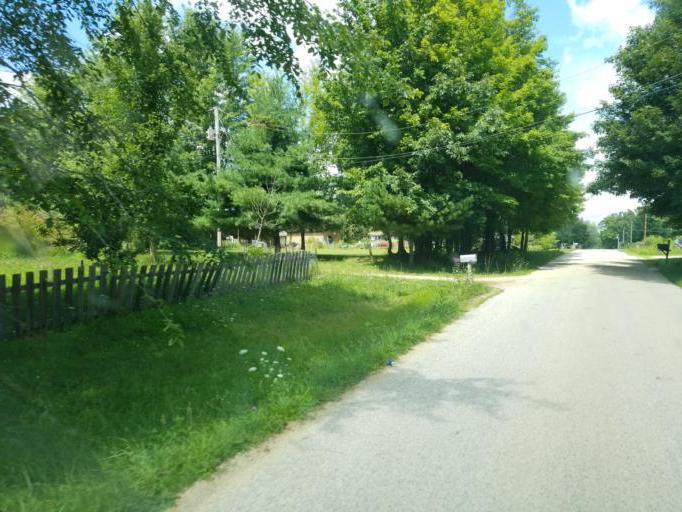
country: US
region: Ohio
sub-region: Knox County
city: Centerburg
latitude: 40.3579
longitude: -82.7785
